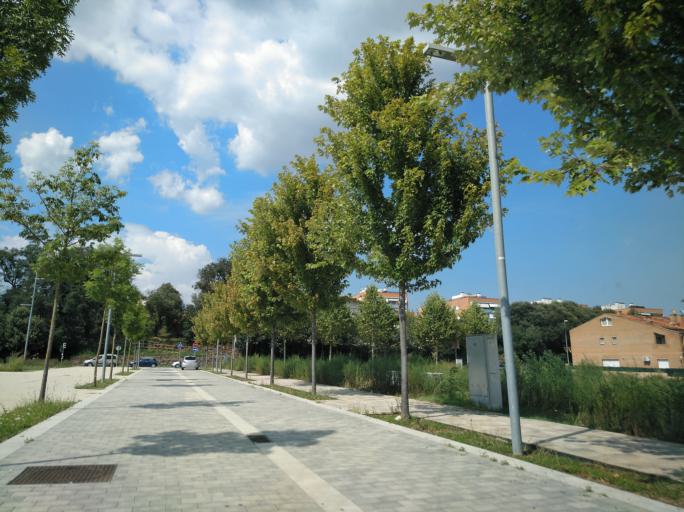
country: ES
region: Catalonia
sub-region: Provincia de Girona
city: Salt
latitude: 41.9910
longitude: 2.8025
